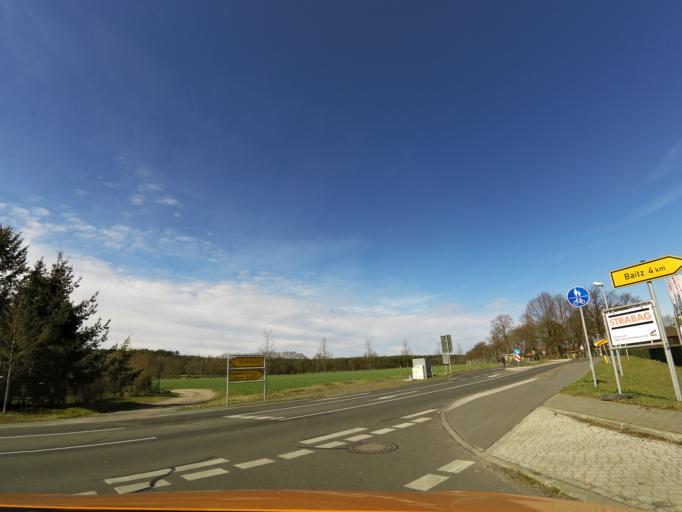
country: DE
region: Brandenburg
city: Belzig
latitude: 52.1798
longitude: 12.6243
